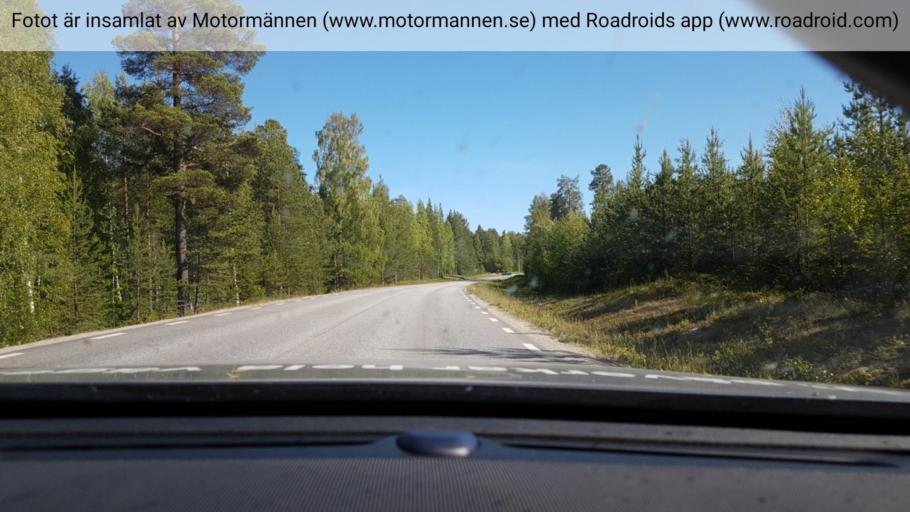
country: SE
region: Vaesterbotten
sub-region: Lycksele Kommun
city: Lycksele
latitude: 64.6237
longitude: 18.6345
